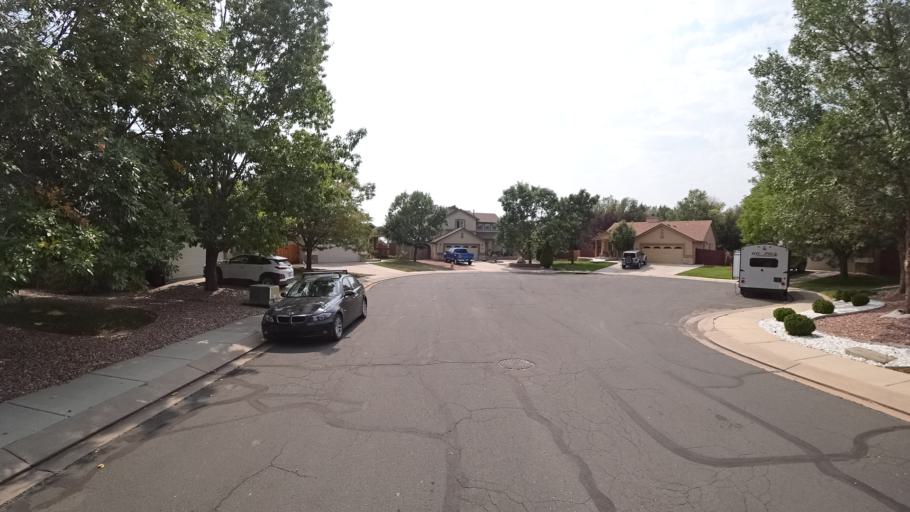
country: US
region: Colorado
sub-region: El Paso County
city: Stratmoor
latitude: 38.8183
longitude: -104.7421
